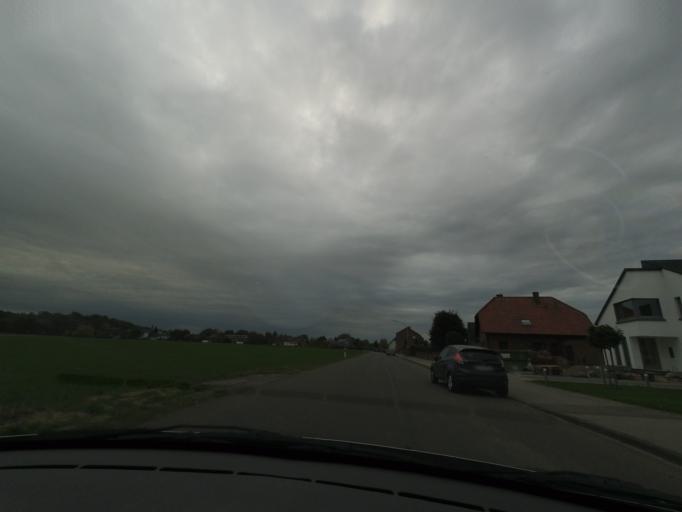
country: DE
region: North Rhine-Westphalia
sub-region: Regierungsbezirk Dusseldorf
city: Korschenbroich
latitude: 51.1711
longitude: 6.5426
